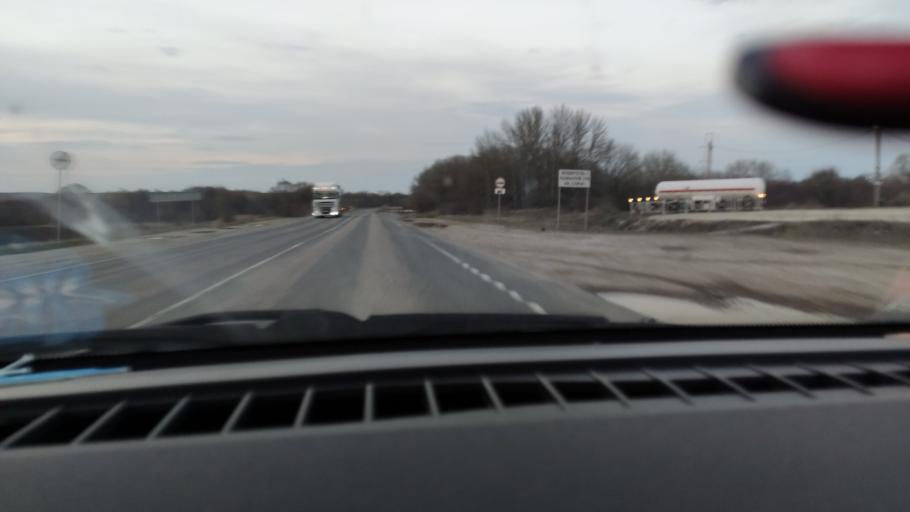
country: RU
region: Saratov
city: Sinodskoye
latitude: 51.9778
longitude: 46.6503
